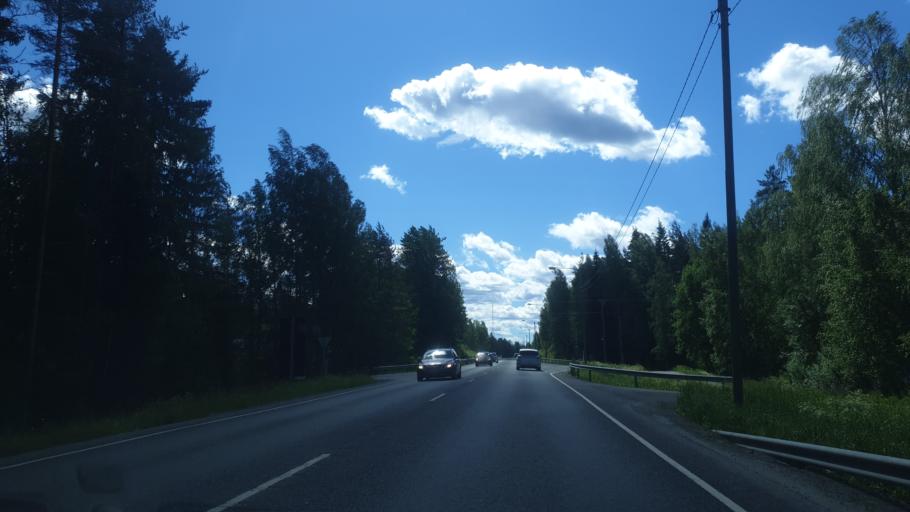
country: FI
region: Northern Savo
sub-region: Varkaus
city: Leppaevirta
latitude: 62.5896
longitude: 27.6050
